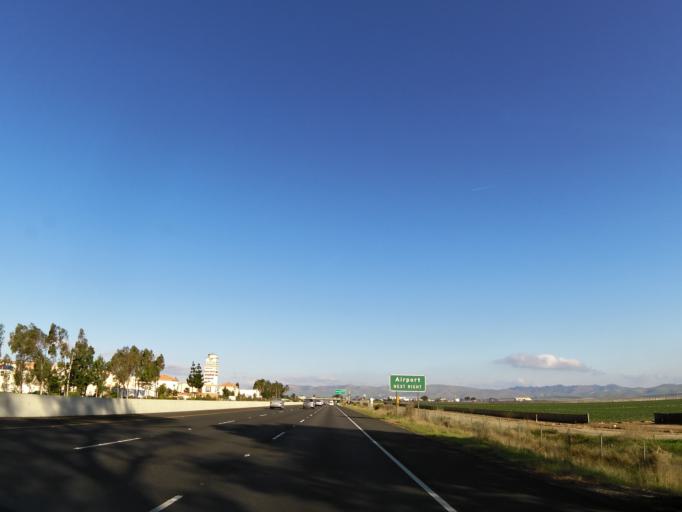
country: US
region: California
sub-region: Santa Barbara County
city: Santa Maria
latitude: 34.9169
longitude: -120.4178
